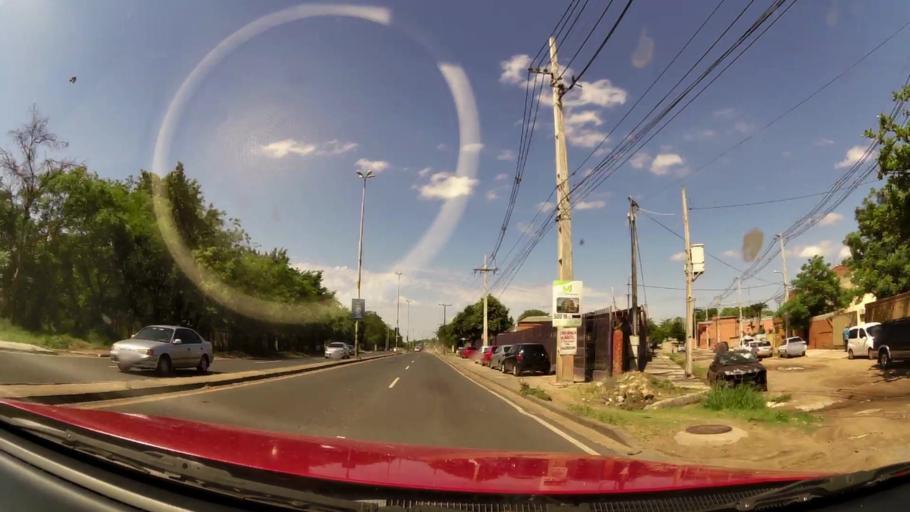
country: PY
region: Asuncion
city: Asuncion
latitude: -25.2552
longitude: -57.5636
